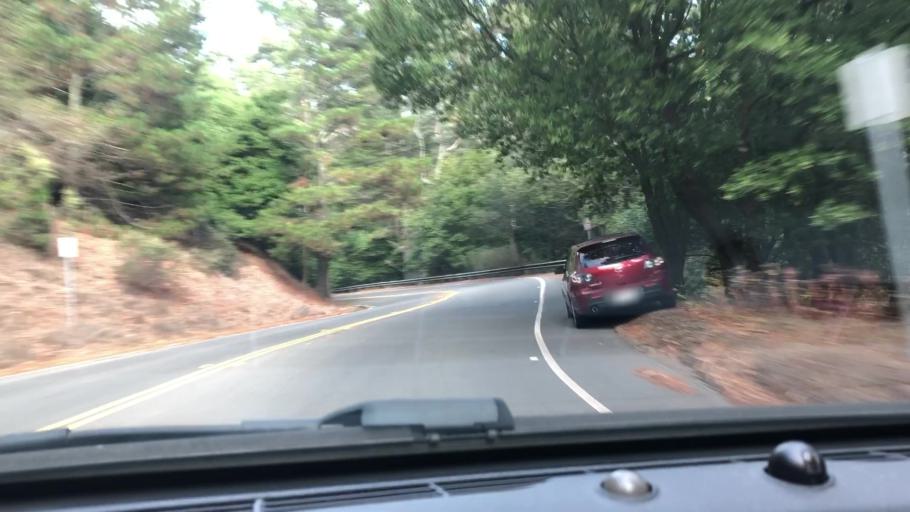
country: US
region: California
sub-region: Alameda County
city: Berkeley
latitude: 37.8816
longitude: -122.2425
